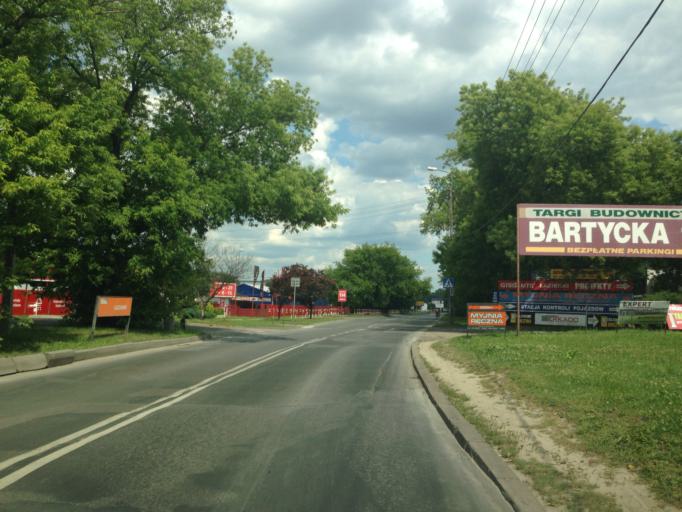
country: PL
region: Masovian Voivodeship
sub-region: Warszawa
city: Mokotow
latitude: 52.2123
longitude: 21.0497
